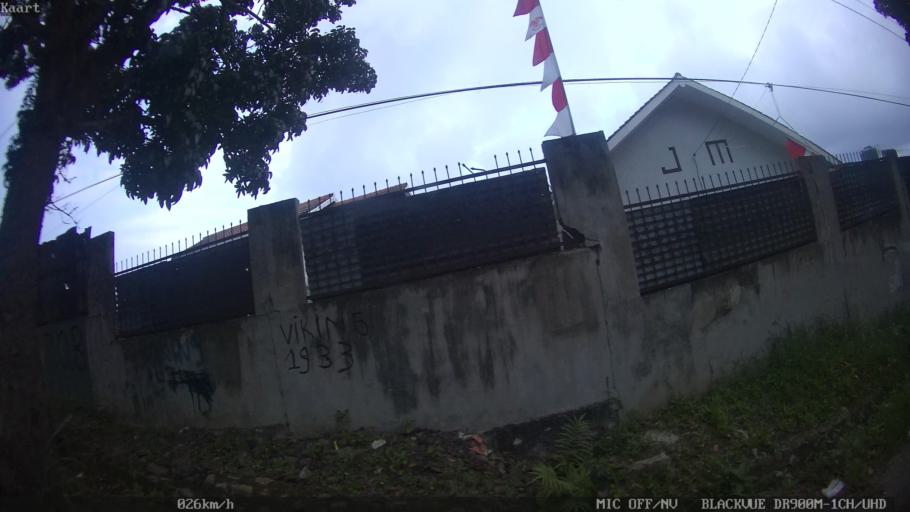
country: ID
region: Lampung
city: Bandarlampung
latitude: -5.4095
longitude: 105.2890
